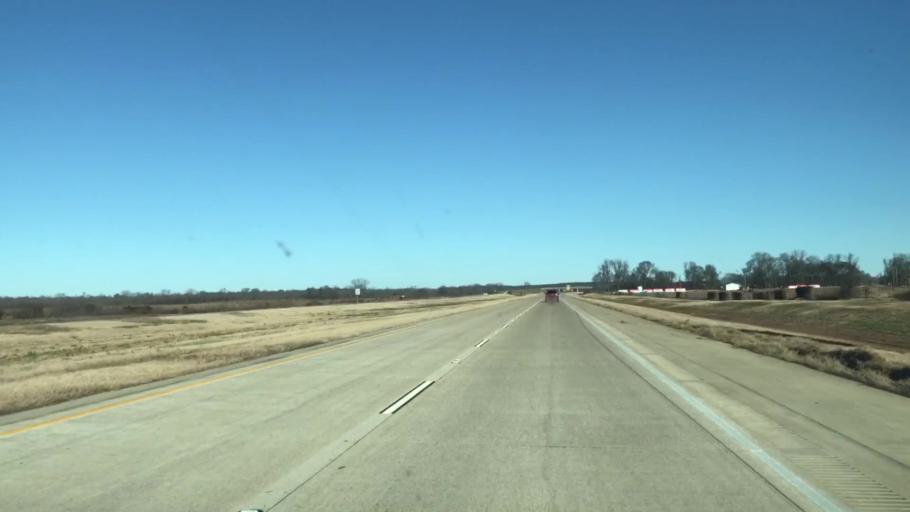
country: US
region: Louisiana
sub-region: Caddo Parish
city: Oil City
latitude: 32.7555
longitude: -93.8837
